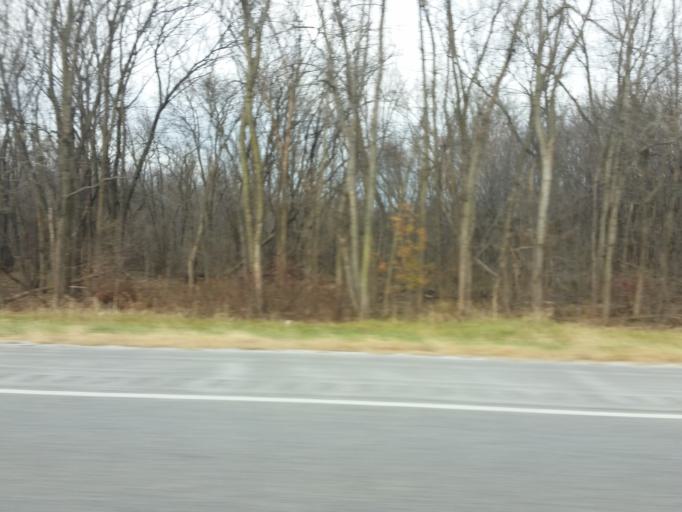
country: US
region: Illinois
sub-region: Rock Island County
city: Carbon Cliff
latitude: 41.4628
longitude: -90.3945
